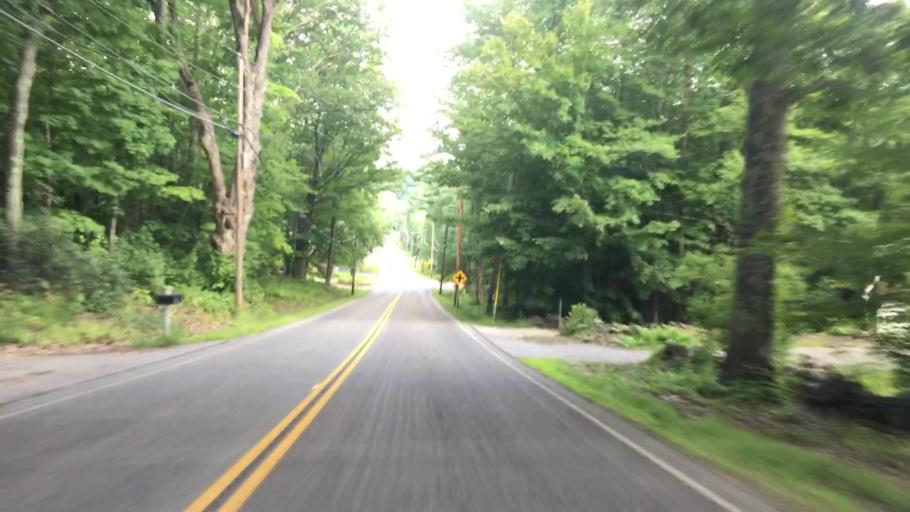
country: US
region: New Hampshire
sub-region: Belknap County
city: Sanbornton
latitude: 43.4934
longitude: -71.5894
